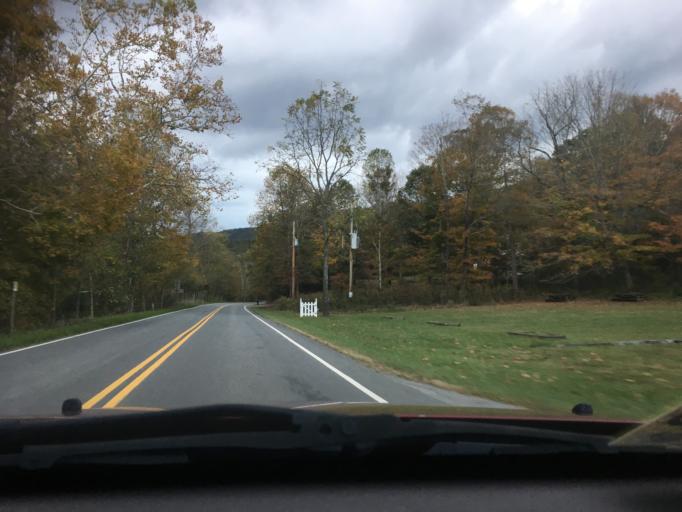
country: US
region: Virginia
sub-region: Giles County
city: Narrows
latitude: 37.2073
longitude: -80.7958
